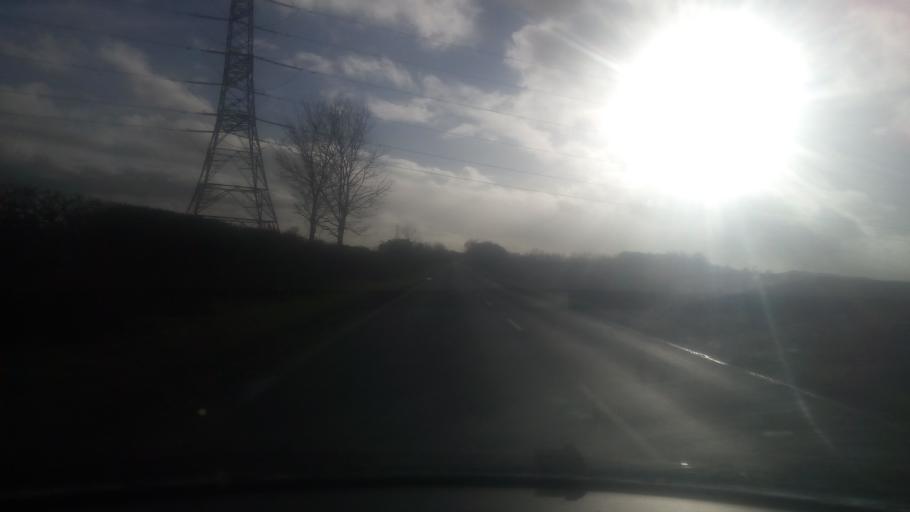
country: GB
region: Scotland
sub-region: The Scottish Borders
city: Kelso
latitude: 55.6740
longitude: -2.3634
